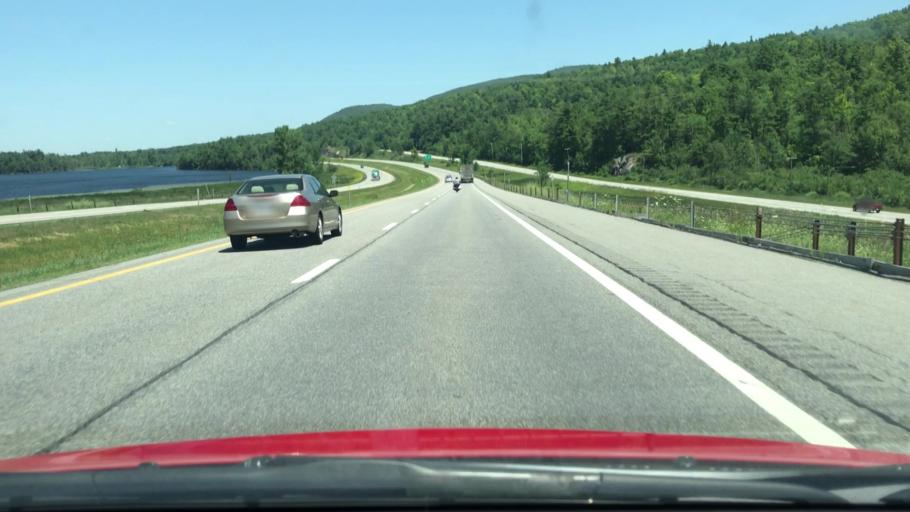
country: US
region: New York
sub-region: Essex County
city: Keeseville
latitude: 44.4207
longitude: -73.4952
